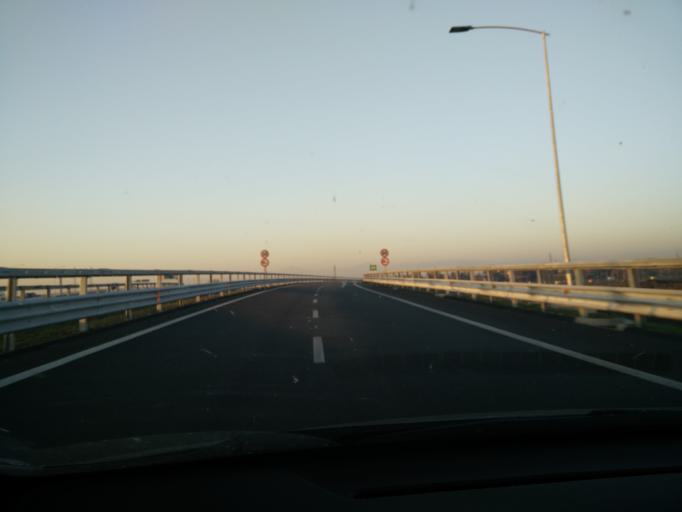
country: IT
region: Lombardy
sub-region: Citta metropolitana di Milano
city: Pozzuolo Martesana
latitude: 45.5005
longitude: 9.4450
